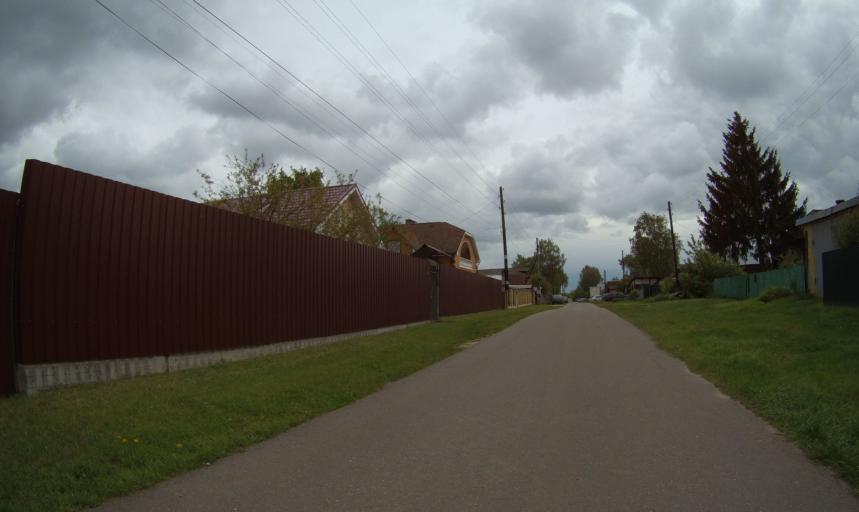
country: RU
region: Moskovskaya
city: Raduzhnyy
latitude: 55.1180
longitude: 38.7621
